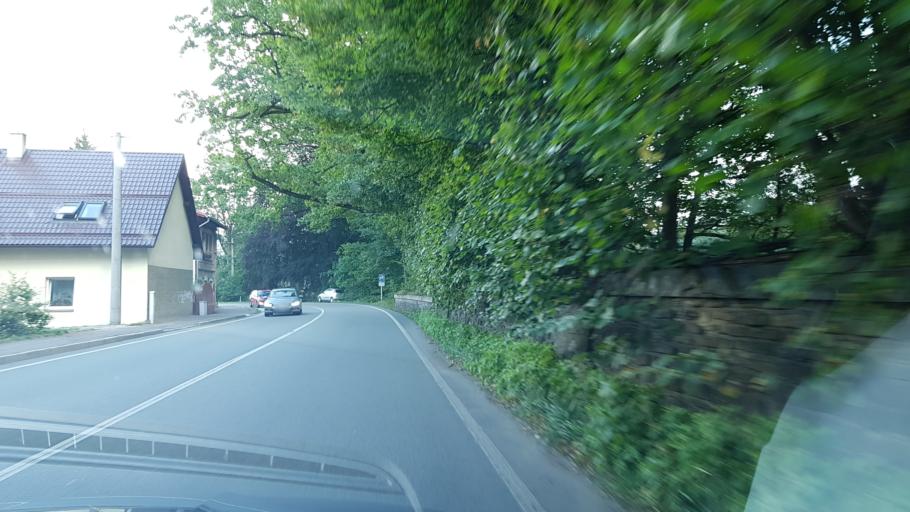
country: CZ
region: Pardubicky
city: Zamberk
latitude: 50.0858
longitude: 16.4701
